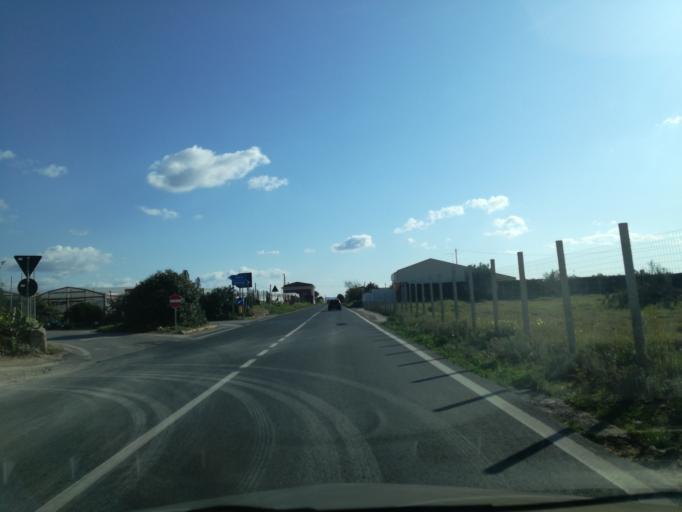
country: IT
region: Sicily
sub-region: Ragusa
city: Acate
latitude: 36.9715
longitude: 14.4755
